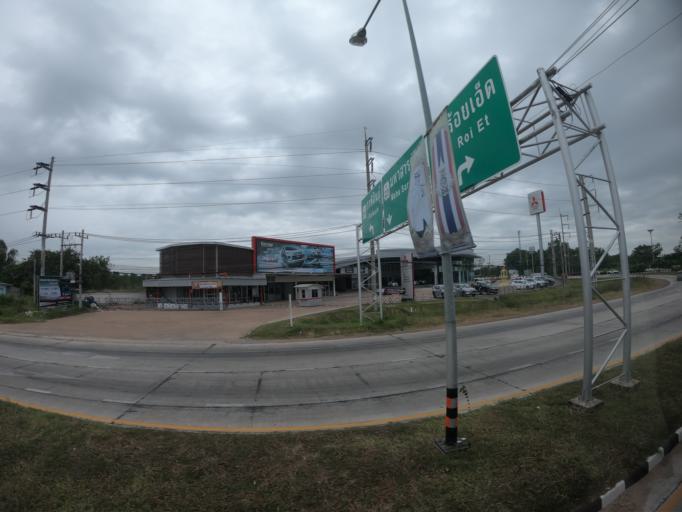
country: TH
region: Maha Sarakham
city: Maha Sarakham
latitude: 16.1636
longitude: 103.2835
